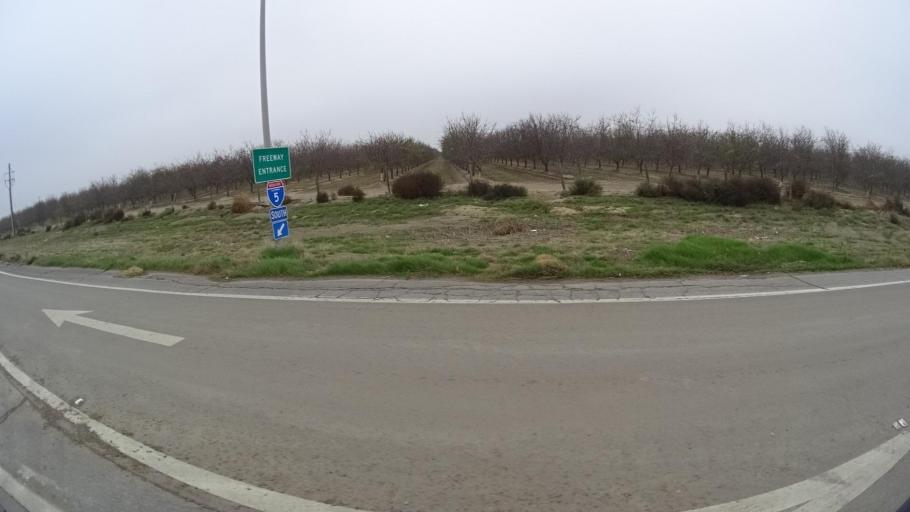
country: US
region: California
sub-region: Kern County
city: Greenfield
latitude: 35.2091
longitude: -119.1664
